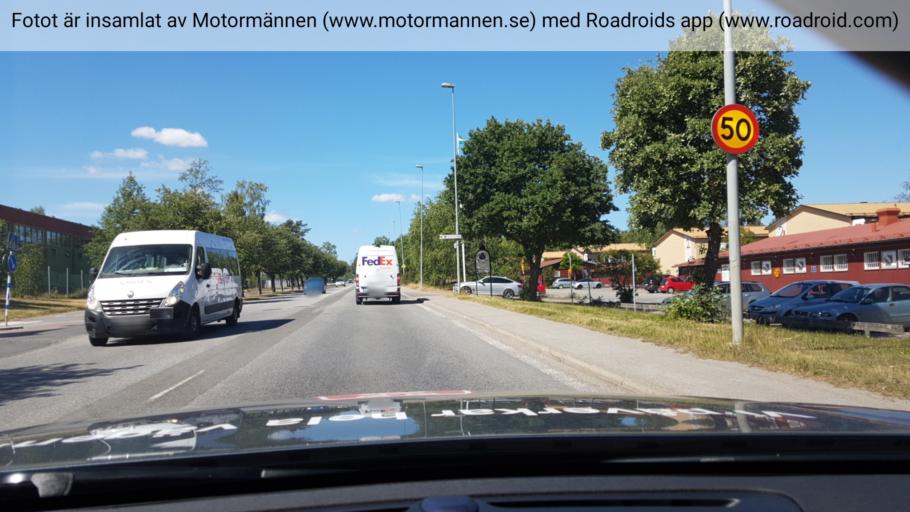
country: SE
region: Stockholm
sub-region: Tyreso Kommun
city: Bollmora
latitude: 59.2430
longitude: 18.2116
